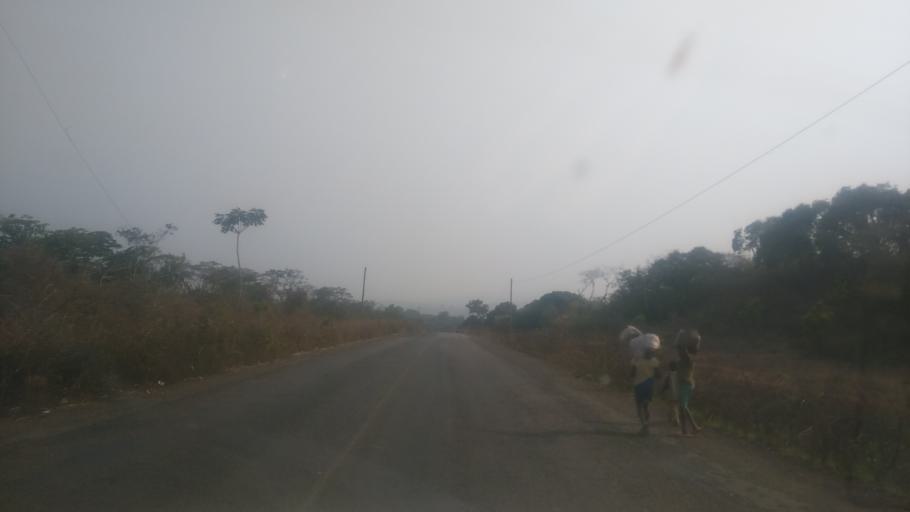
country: CM
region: West
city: Tonga
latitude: 5.0280
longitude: 10.6971
